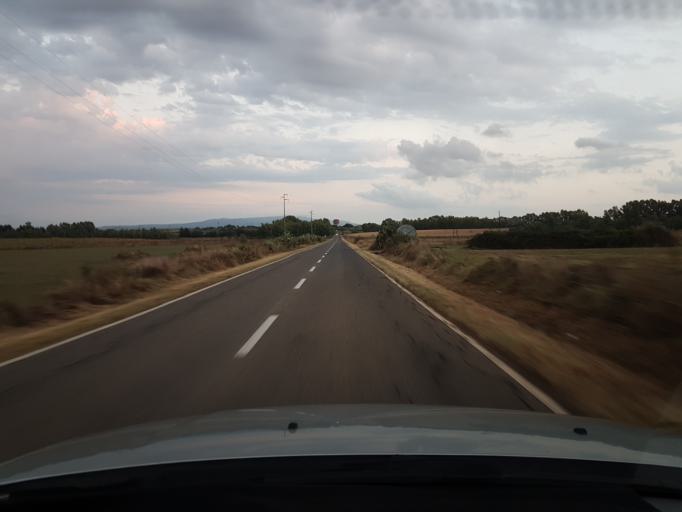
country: IT
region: Sardinia
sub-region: Provincia di Oristano
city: Tramatza
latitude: 40.0155
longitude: 8.6442
